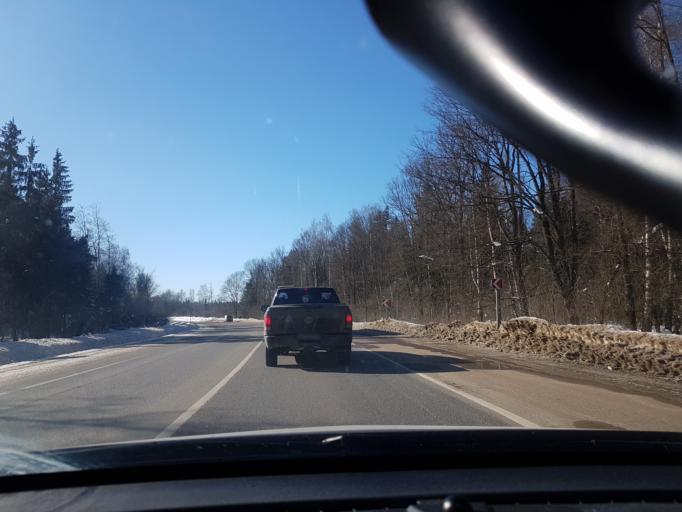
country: RU
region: Moskovskaya
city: Kostrovo
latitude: 55.9142
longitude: 36.7372
